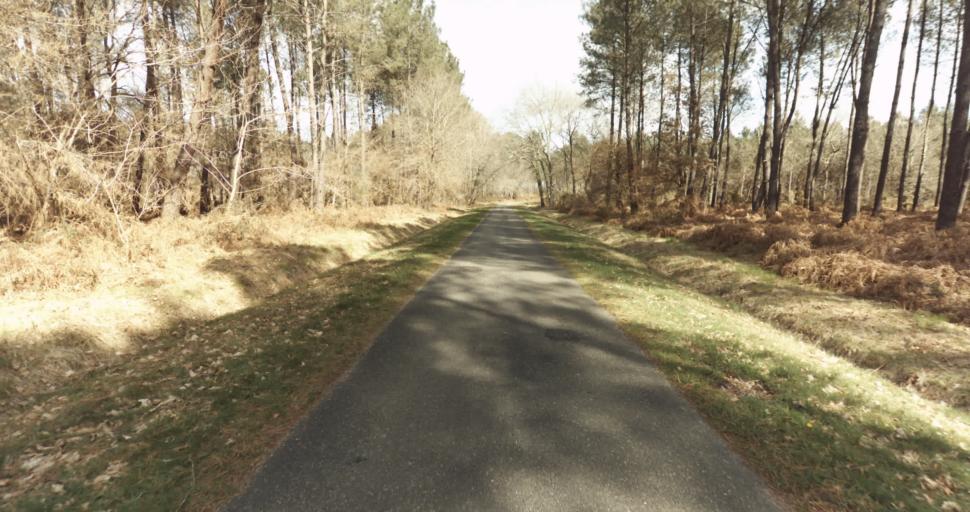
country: FR
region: Aquitaine
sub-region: Departement des Landes
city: Roquefort
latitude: 44.0584
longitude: -0.3377
